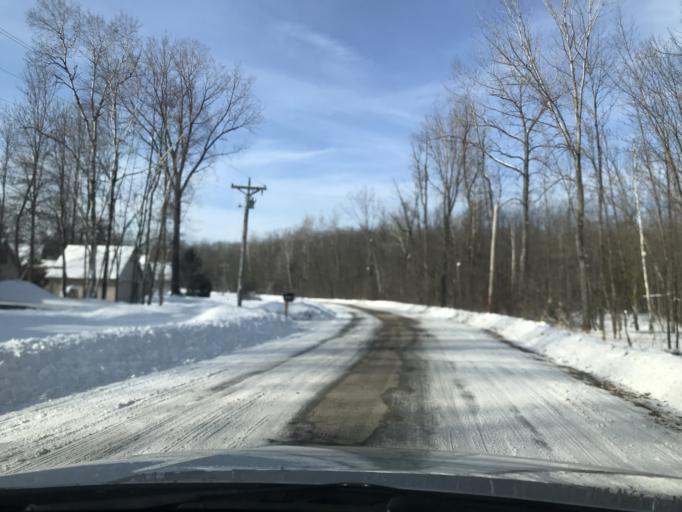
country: US
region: Wisconsin
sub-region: Oconto County
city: Oconto Falls
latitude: 45.1562
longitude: -88.1943
